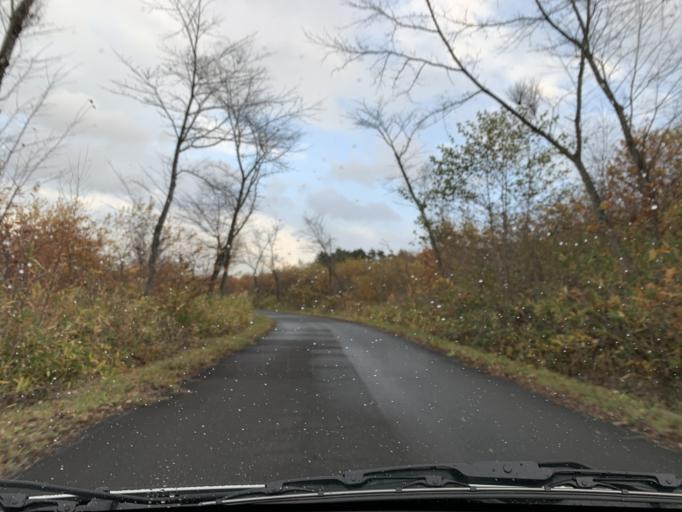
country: JP
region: Iwate
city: Mizusawa
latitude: 39.0827
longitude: 141.0173
